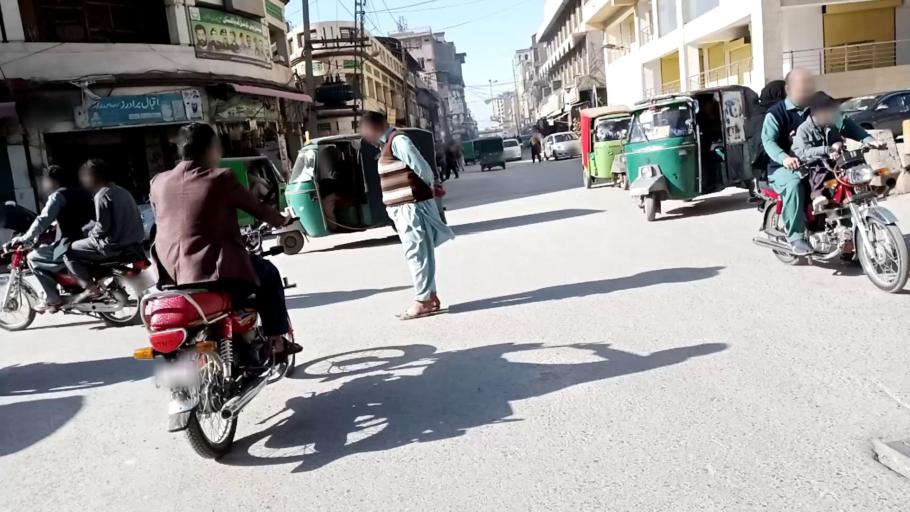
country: PK
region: Khyber Pakhtunkhwa
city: Peshawar
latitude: 34.0042
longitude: 71.5668
